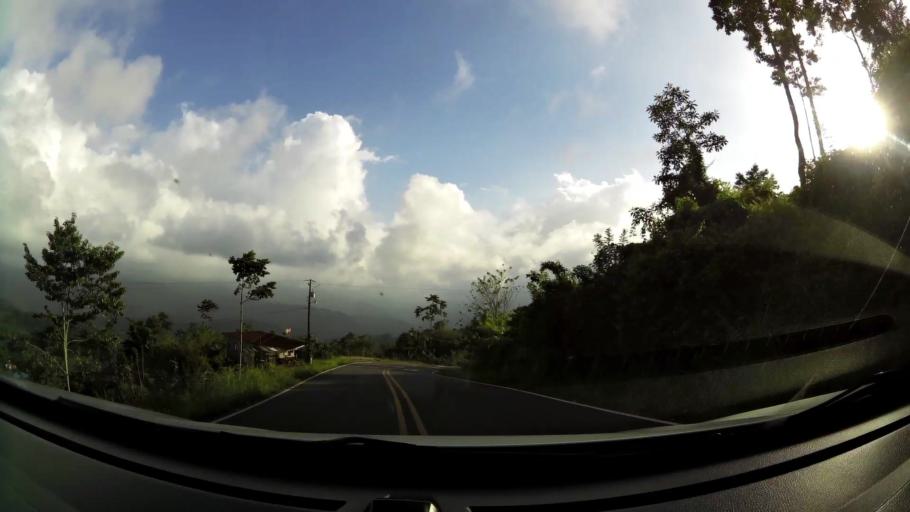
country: CR
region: Limon
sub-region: Canton de Siquirres
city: Siquirres
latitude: 10.0366
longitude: -83.5480
